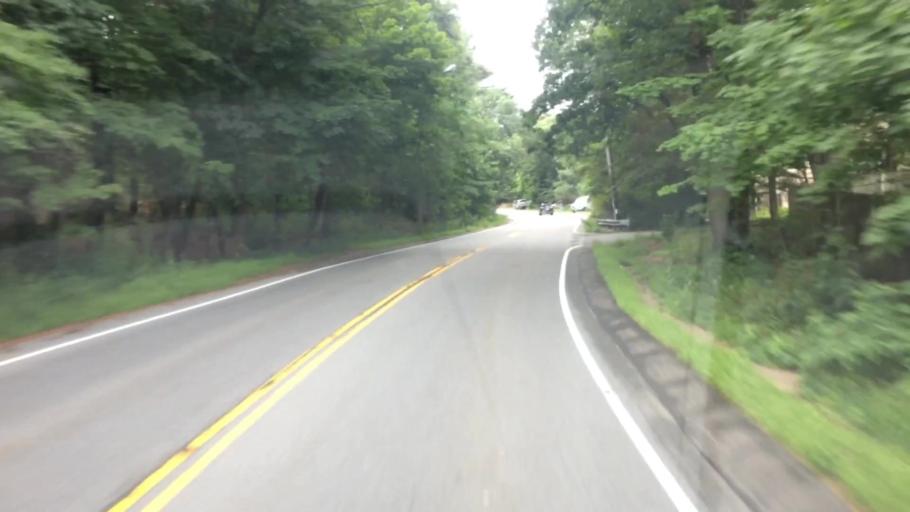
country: US
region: Massachusetts
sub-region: Middlesex County
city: Winchester
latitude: 42.4442
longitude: -71.1243
